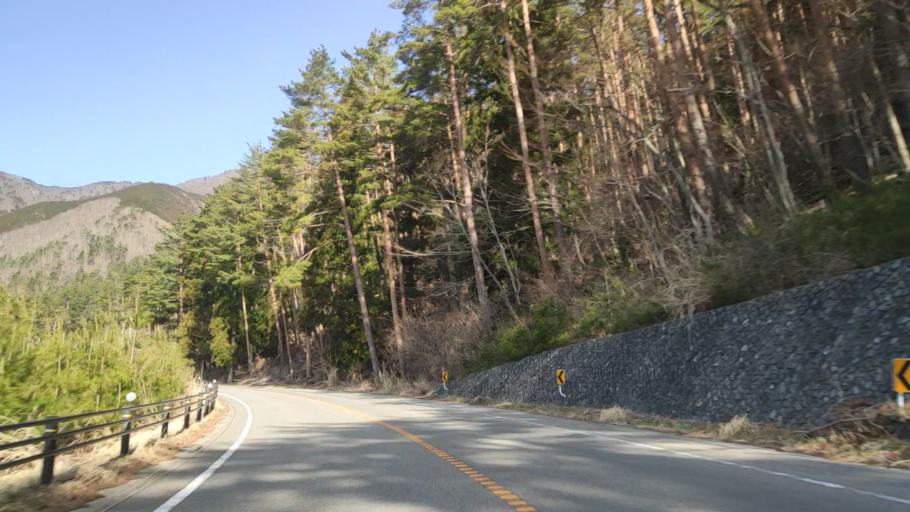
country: JP
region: Yamanashi
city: Fujikawaguchiko
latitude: 35.5275
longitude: 138.7178
